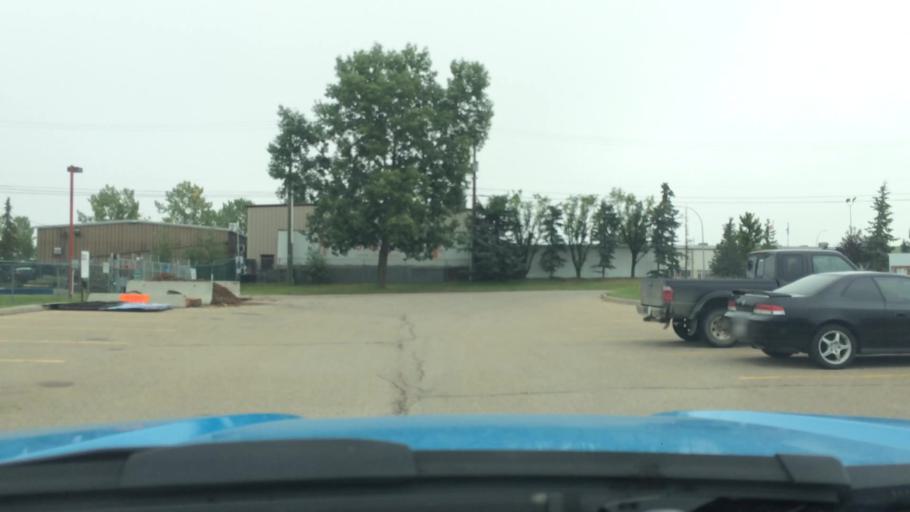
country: CA
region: Alberta
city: Airdrie
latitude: 51.2876
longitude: -113.9830
